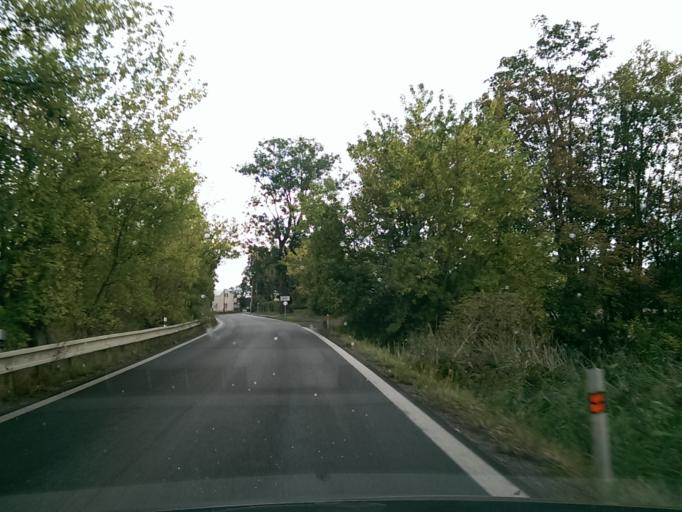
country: CZ
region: Central Bohemia
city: Bakov nad Jizerou
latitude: 50.4831
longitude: 14.9841
